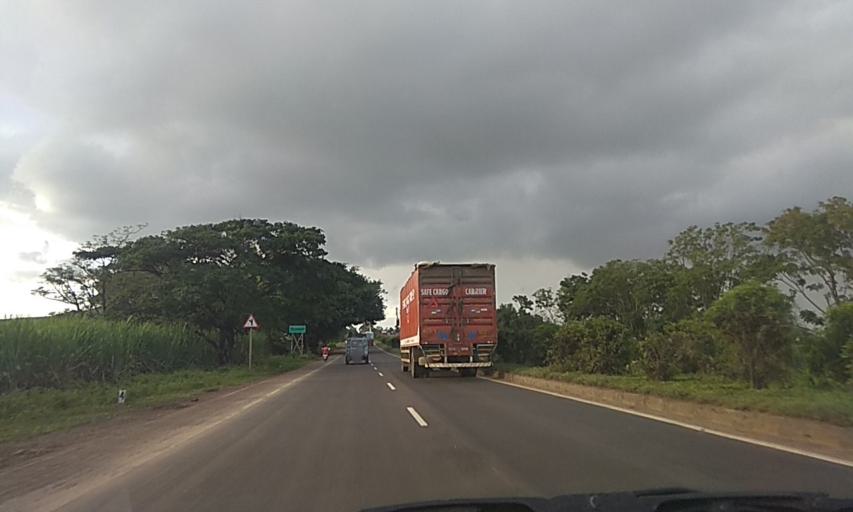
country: IN
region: Maharashtra
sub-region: Satara Division
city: Rahimatpur
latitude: 17.4938
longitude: 74.0823
